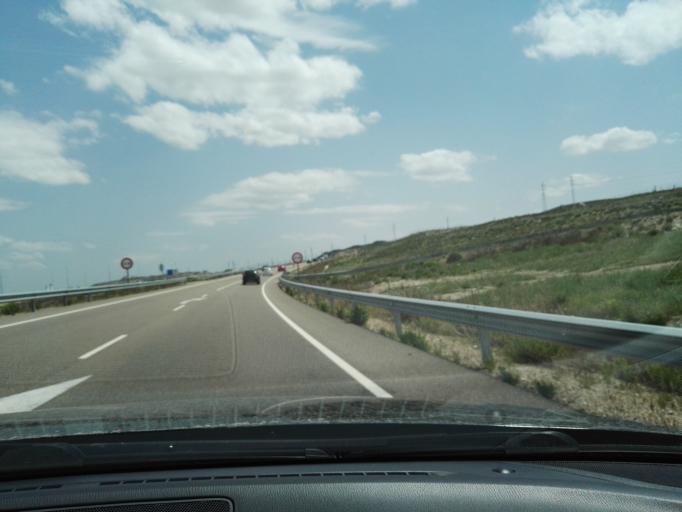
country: ES
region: Aragon
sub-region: Provincia de Zaragoza
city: Montecanal
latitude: 41.6210
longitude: -0.9729
